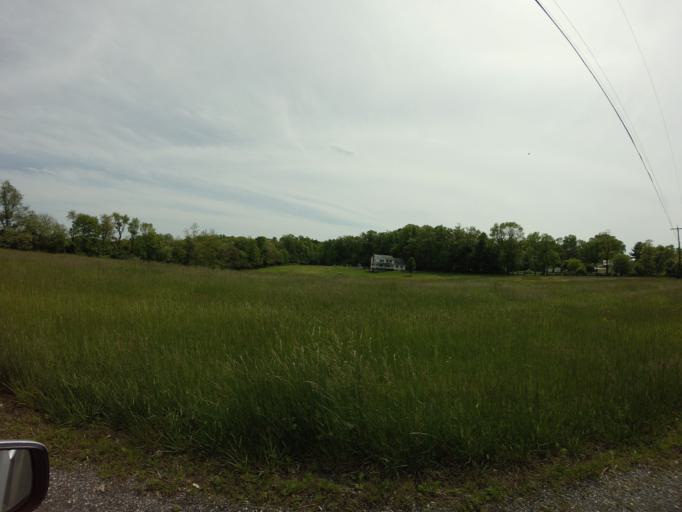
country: US
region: Maryland
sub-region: Carroll County
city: New Windsor
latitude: 39.4687
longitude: -77.0390
